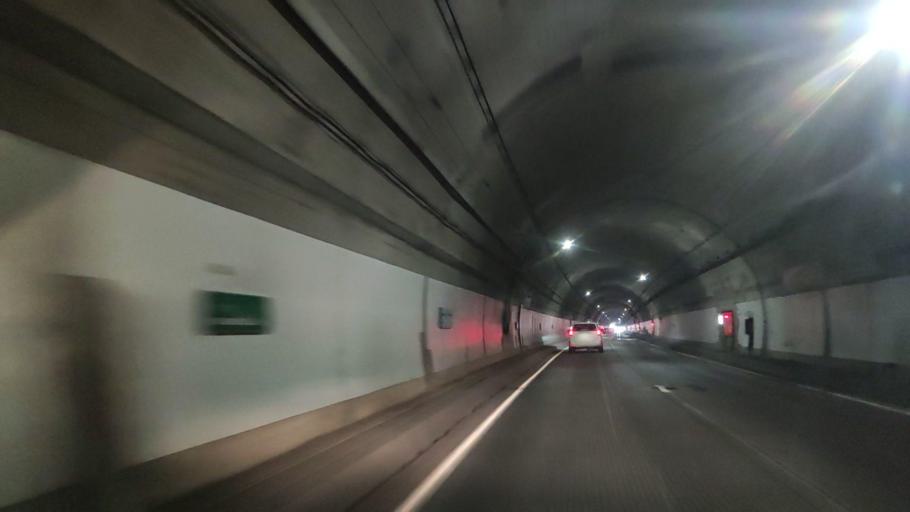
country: JP
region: Hokkaido
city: Rumoi
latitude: 43.7000
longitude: 141.3377
